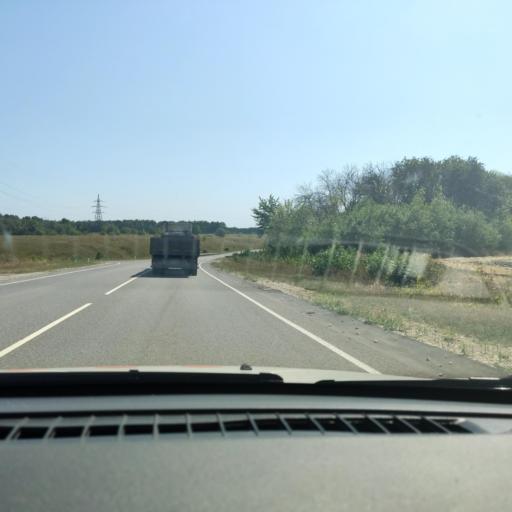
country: RU
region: Voronezj
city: Ostrogozhsk
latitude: 50.8901
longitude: 39.1035
